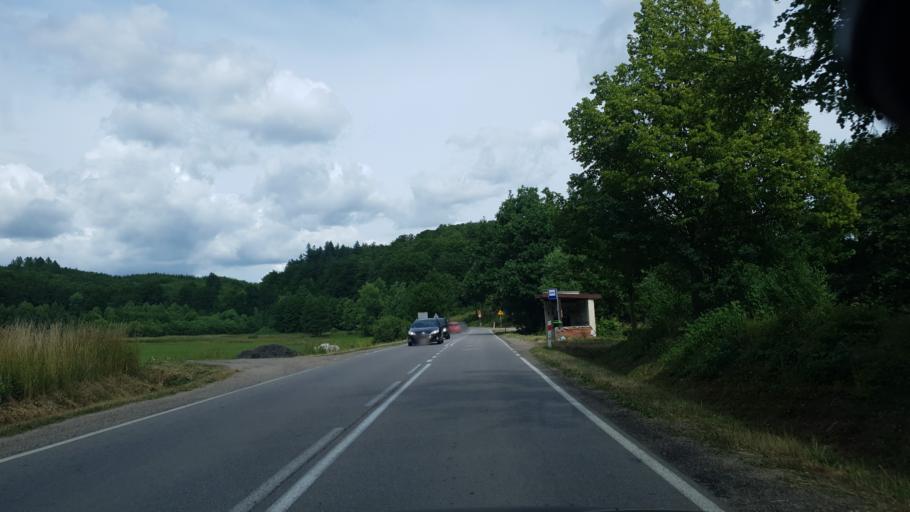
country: PL
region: Pomeranian Voivodeship
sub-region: Powiat kartuski
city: Kartuzy
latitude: 54.3129
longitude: 18.1592
